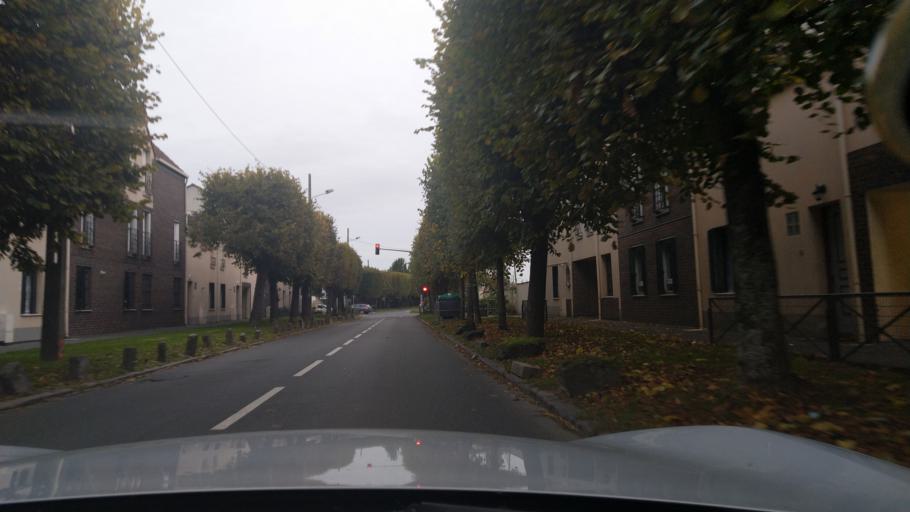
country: FR
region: Ile-de-France
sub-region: Departement de Seine-Saint-Denis
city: Villepinte
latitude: 48.9773
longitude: 2.5575
